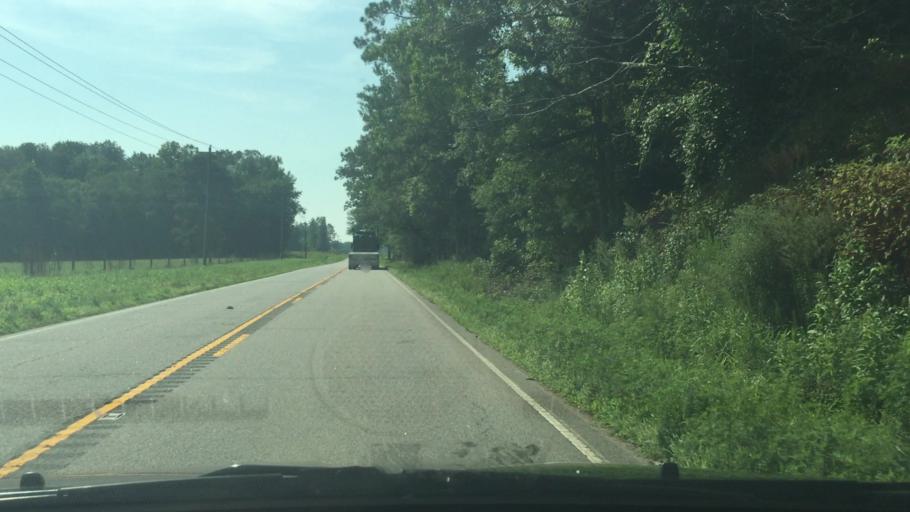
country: US
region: Virginia
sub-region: Sussex County
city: Sussex
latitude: 36.9963
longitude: -77.2606
